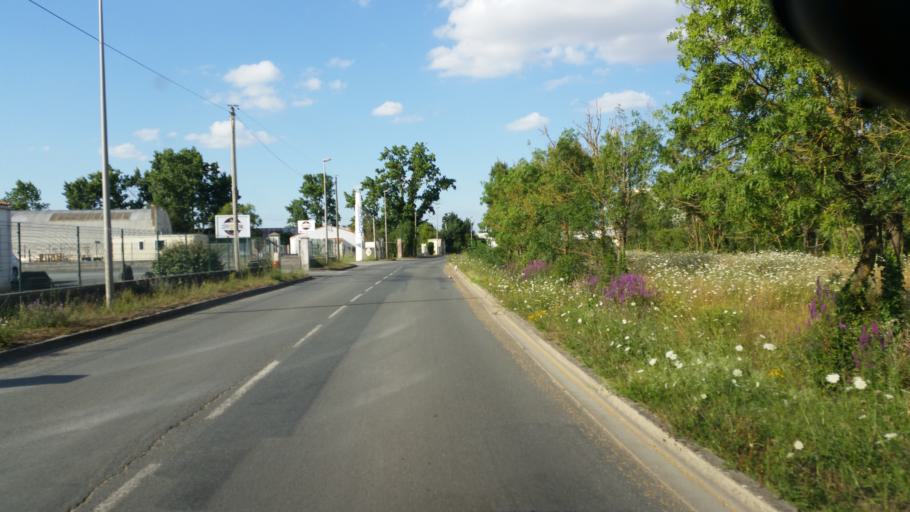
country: FR
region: Poitou-Charentes
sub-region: Departement de la Charente-Maritime
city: Marans
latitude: 46.3117
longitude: -1.0043
